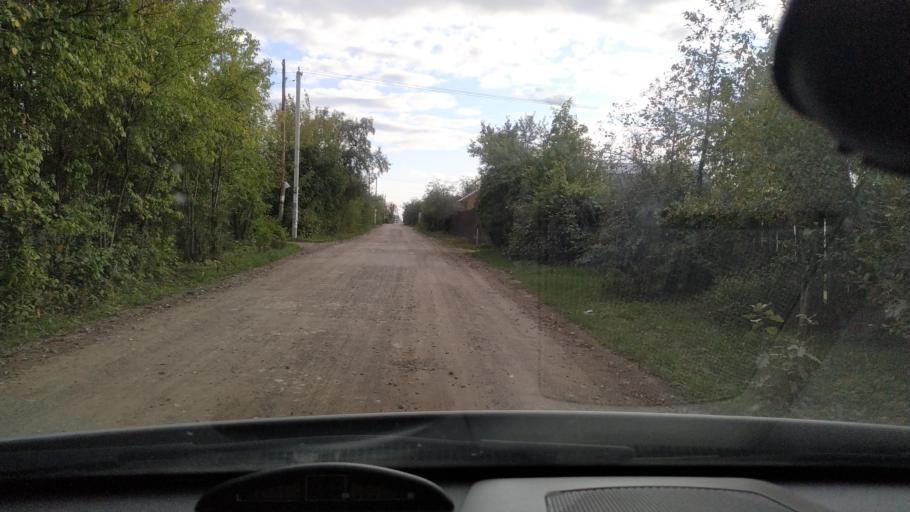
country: RU
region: Rjazan
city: Polyany
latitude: 54.5573
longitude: 39.8760
